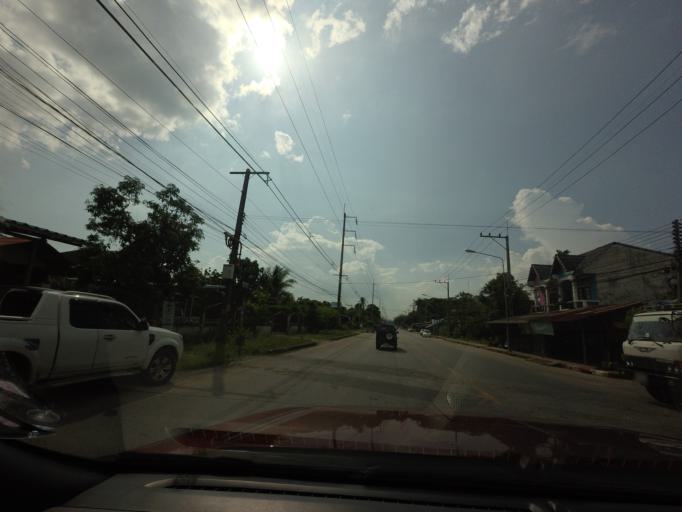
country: TH
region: Yala
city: Yala
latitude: 6.5196
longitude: 101.2681
